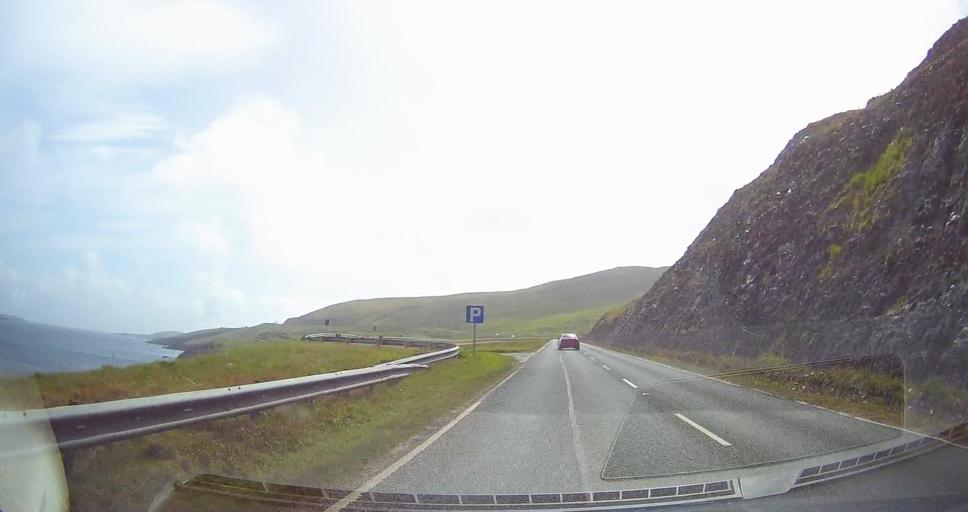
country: GB
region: Scotland
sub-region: Shetland Islands
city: Sandwick
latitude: 60.0311
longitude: -1.2346
